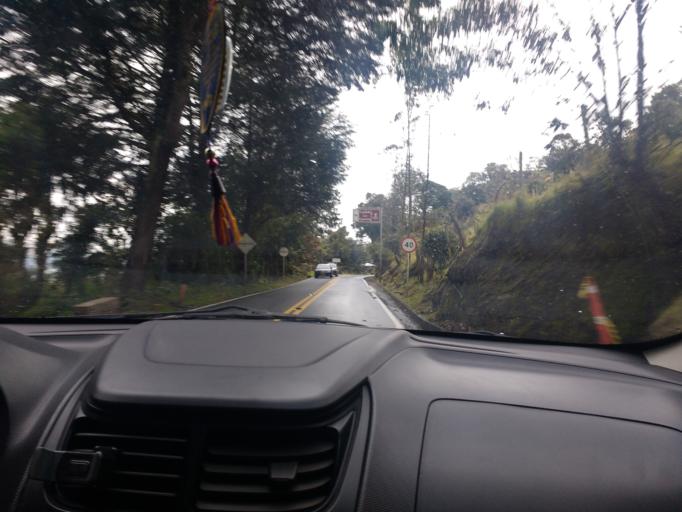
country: CO
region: Cundinamarca
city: Choachi
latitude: 4.5657
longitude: -73.9600
